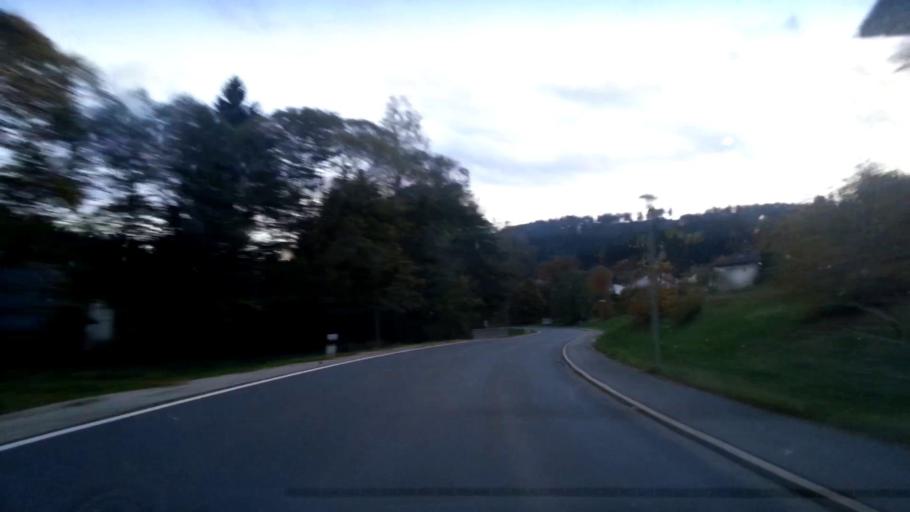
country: DE
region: Bavaria
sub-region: Upper Franconia
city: Warmensteinach
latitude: 49.9878
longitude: 11.7733
